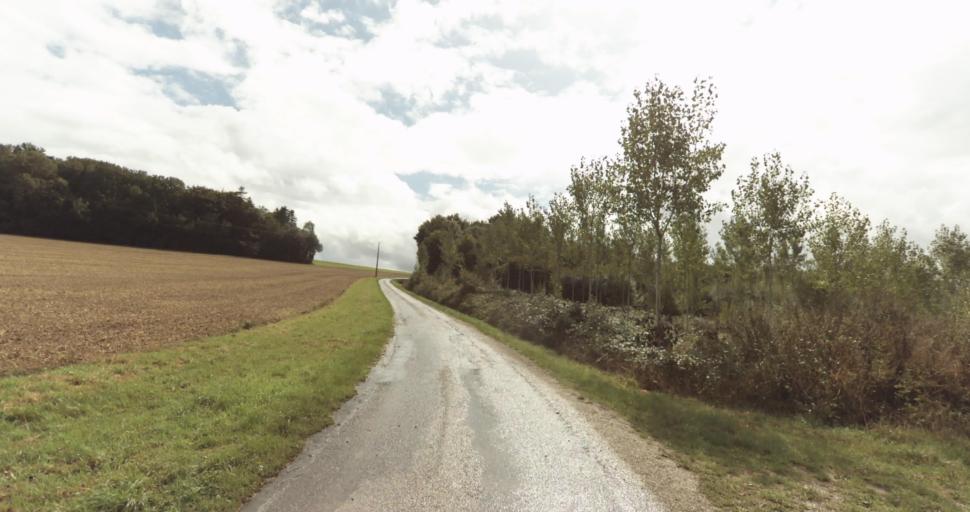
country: FR
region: Lower Normandy
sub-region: Departement de l'Orne
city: Sainte-Gauburge-Sainte-Colombe
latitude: 48.7007
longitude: 0.4070
